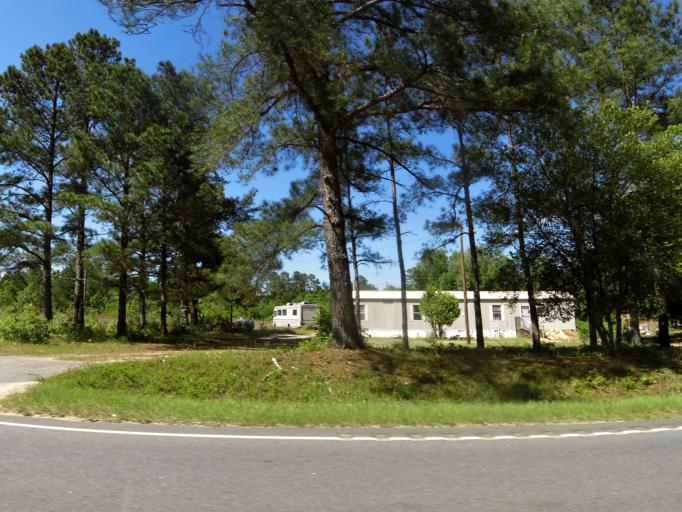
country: US
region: South Carolina
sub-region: Aiken County
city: New Ellenton
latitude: 33.5152
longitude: -81.5807
